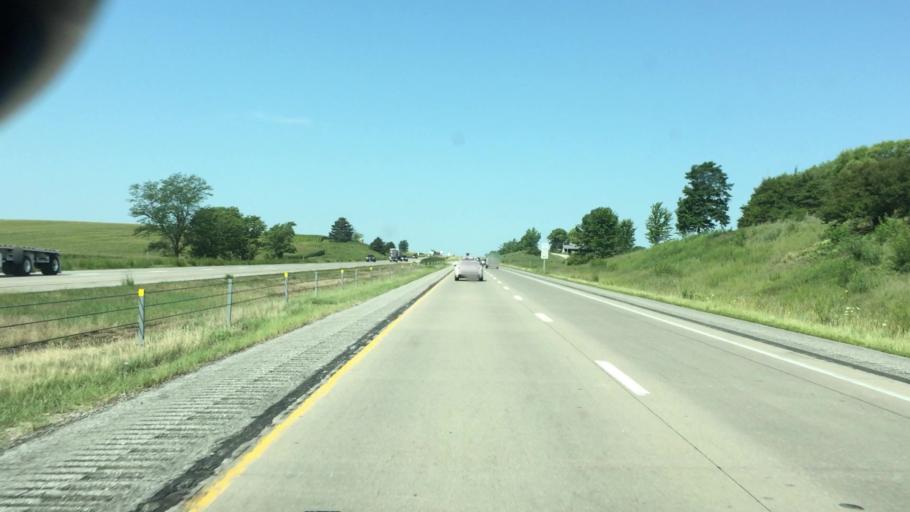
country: US
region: Iowa
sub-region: Iowa County
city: Williamsburg
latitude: 41.6872
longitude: -92.0192
